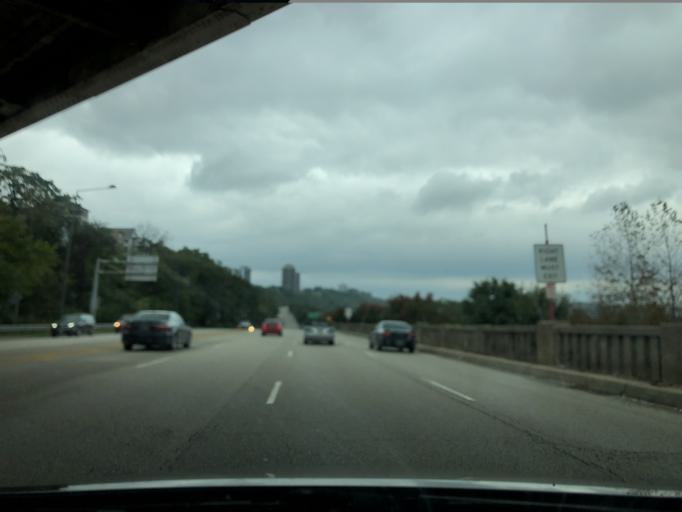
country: US
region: Kentucky
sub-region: Campbell County
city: Bellevue
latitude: 39.1075
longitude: -84.4936
